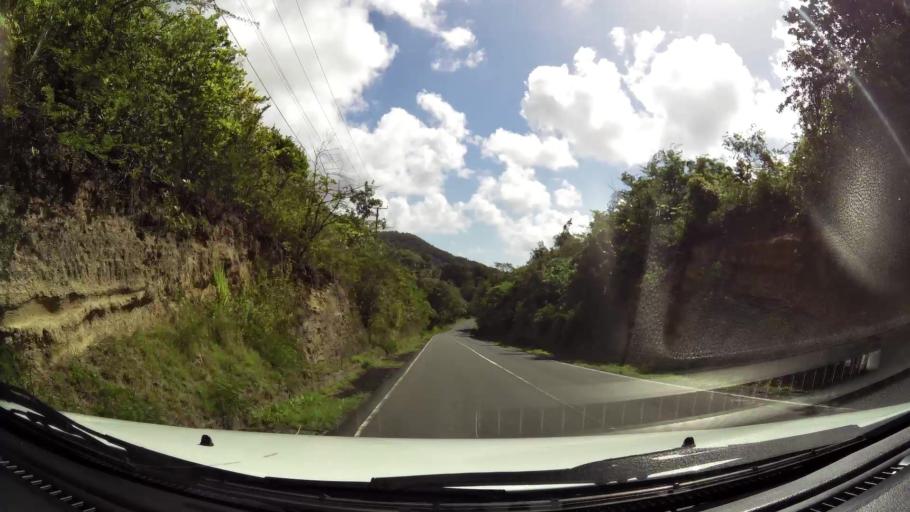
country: LC
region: Laborie Quarter
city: Laborie
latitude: 13.7566
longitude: -61.0149
